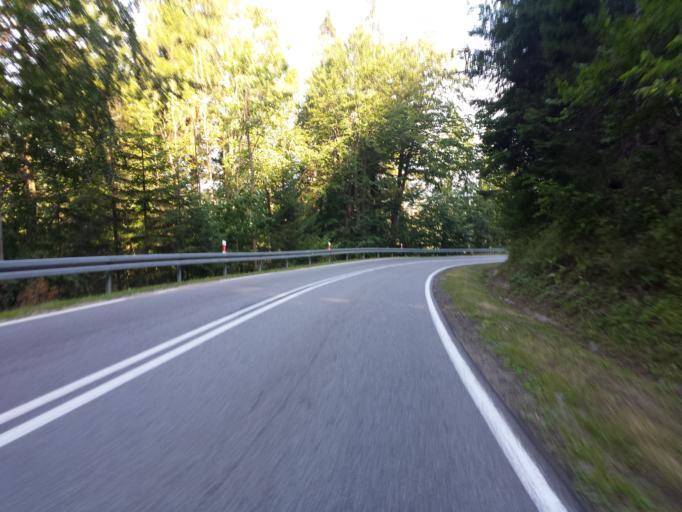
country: PL
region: Subcarpathian Voivodeship
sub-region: Powiat leski
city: Cisna
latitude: 49.2490
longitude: 22.2885
